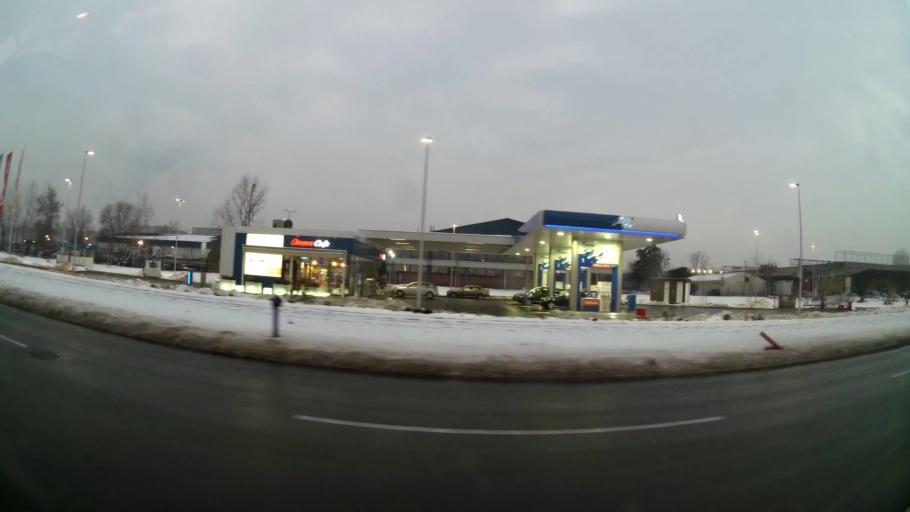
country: RS
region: Central Serbia
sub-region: Belgrade
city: Novi Beograd
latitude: 44.8117
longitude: 20.4054
